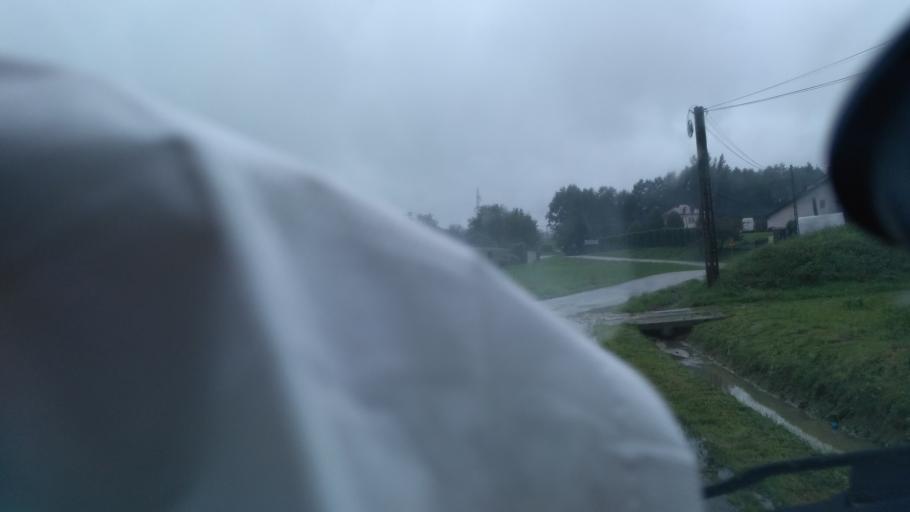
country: PL
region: Subcarpathian Voivodeship
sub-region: Powiat ropczycko-sedziszowski
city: Niedzwiada
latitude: 50.0271
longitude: 21.5418
